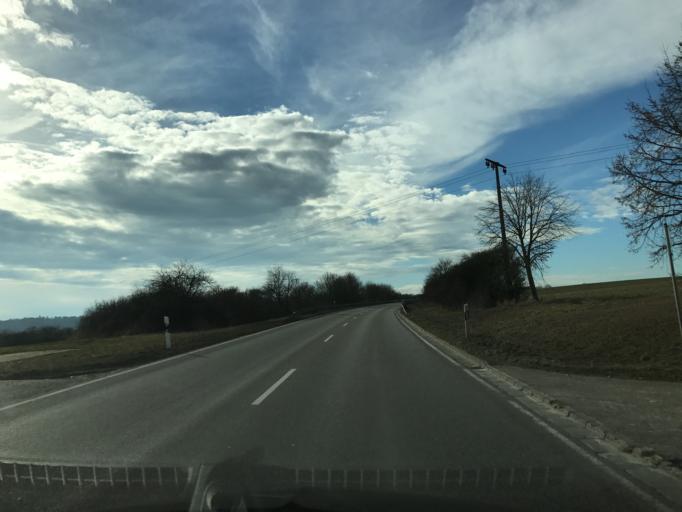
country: DE
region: Baden-Wuerttemberg
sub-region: Regierungsbezirk Stuttgart
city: Giengen an der Brenz
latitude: 48.6036
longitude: 10.2371
